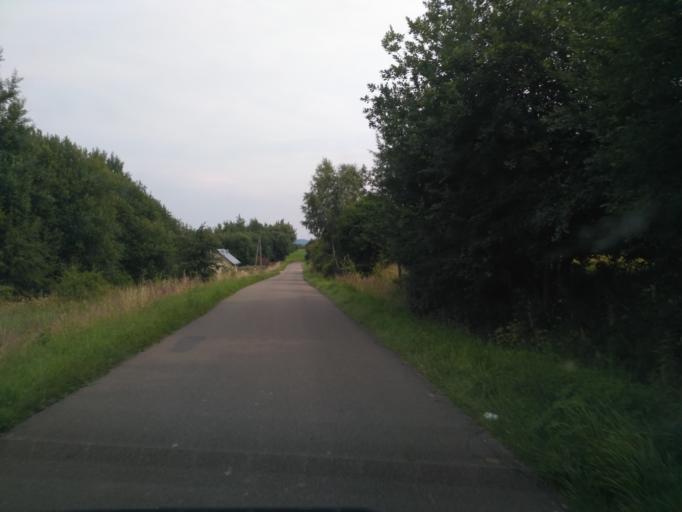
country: PL
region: Subcarpathian Voivodeship
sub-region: Powiat strzyzowski
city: Jawornik
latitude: 49.8613
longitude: 21.8756
